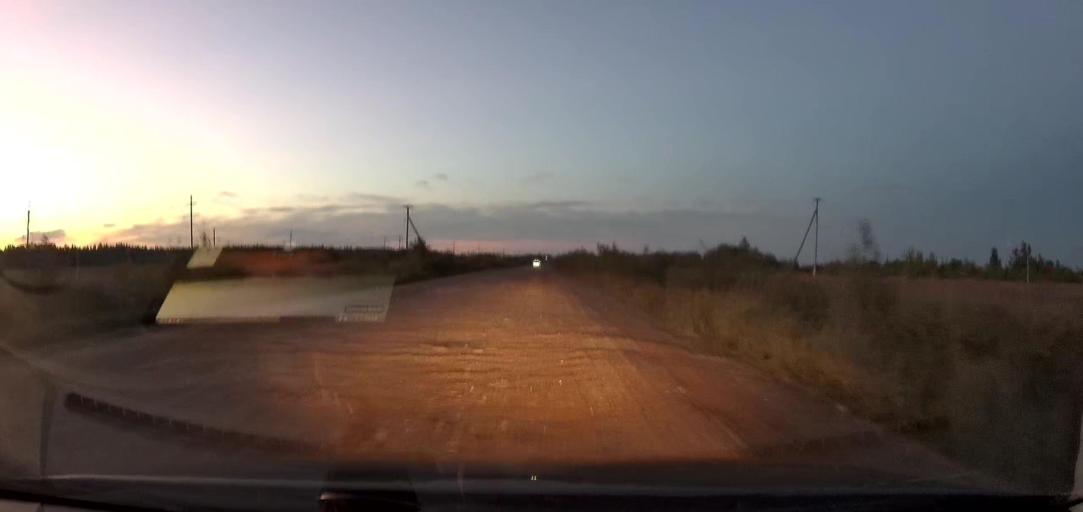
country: RU
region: Arkhangelskaya
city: Kholmogory
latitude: 64.3301
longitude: 41.4435
